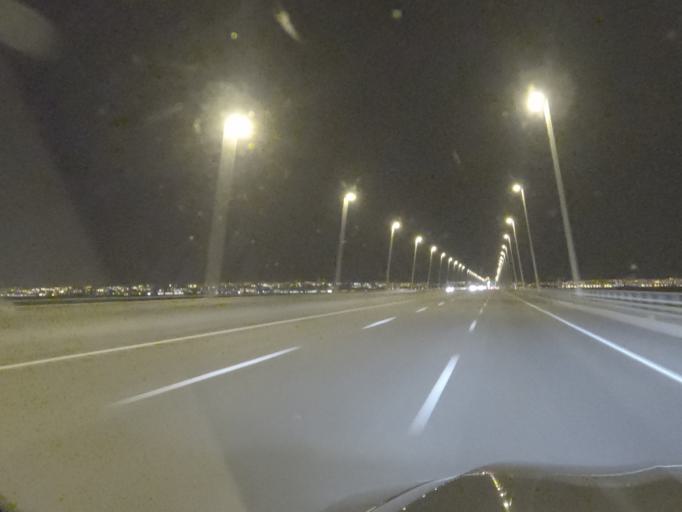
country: PT
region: Setubal
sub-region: Montijo
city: Montijo
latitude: 38.7414
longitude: -9.0149
